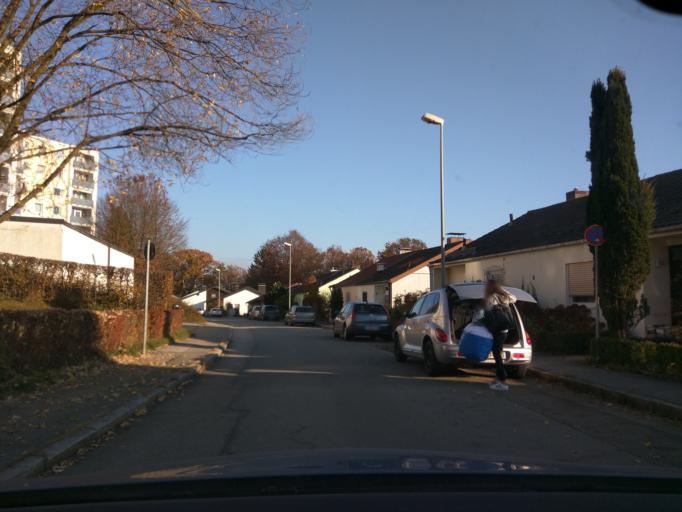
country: DE
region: Bavaria
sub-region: Lower Bavaria
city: Passau
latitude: 48.5604
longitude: 13.4348
